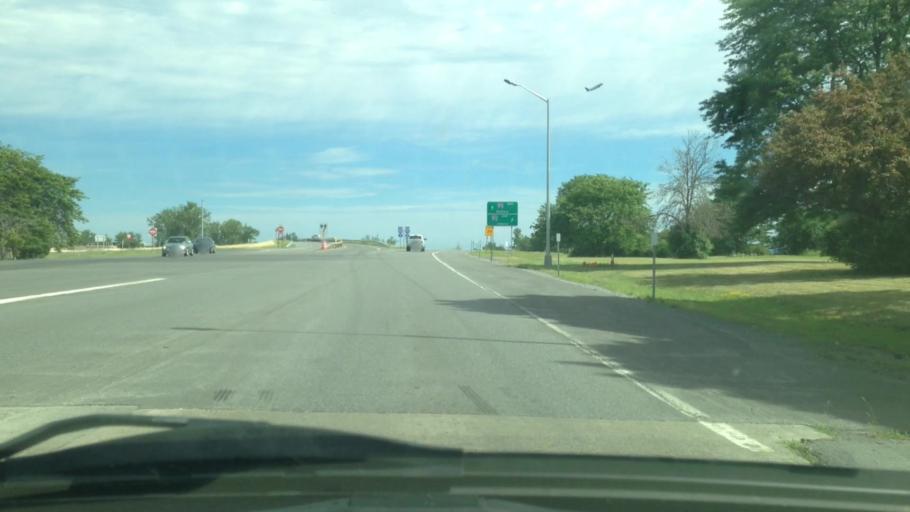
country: US
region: New York
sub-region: Onondaga County
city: East Syracuse
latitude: 43.0903
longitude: -76.0895
